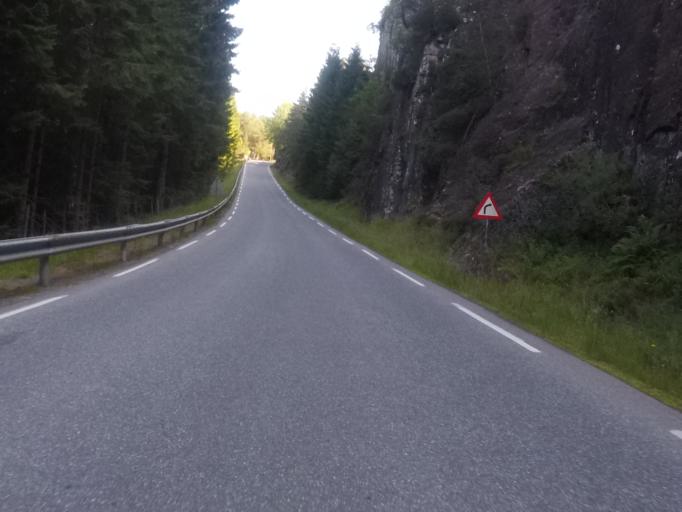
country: NO
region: Sogn og Fjordane
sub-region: Bremanger
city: Svelgen
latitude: 61.7217
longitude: 5.2040
